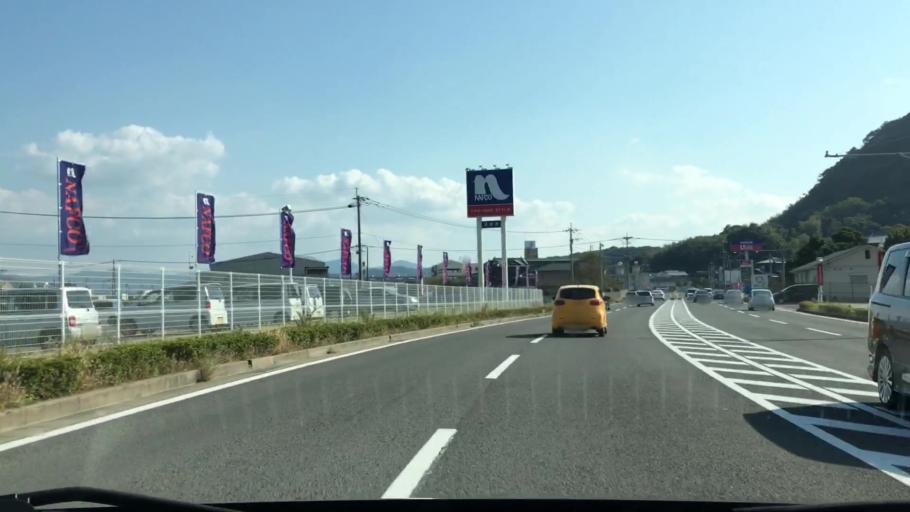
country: JP
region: Nagasaki
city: Togitsu
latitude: 32.8490
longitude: 129.8297
